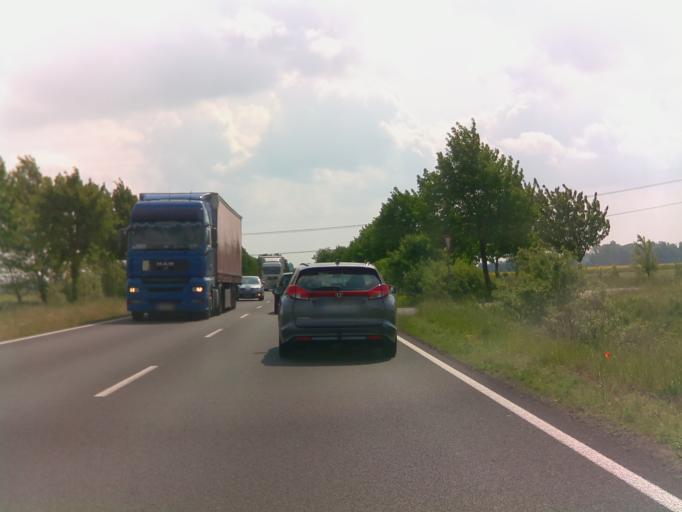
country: DE
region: Saxony-Anhalt
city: Luderitz
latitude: 52.5732
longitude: 11.7220
